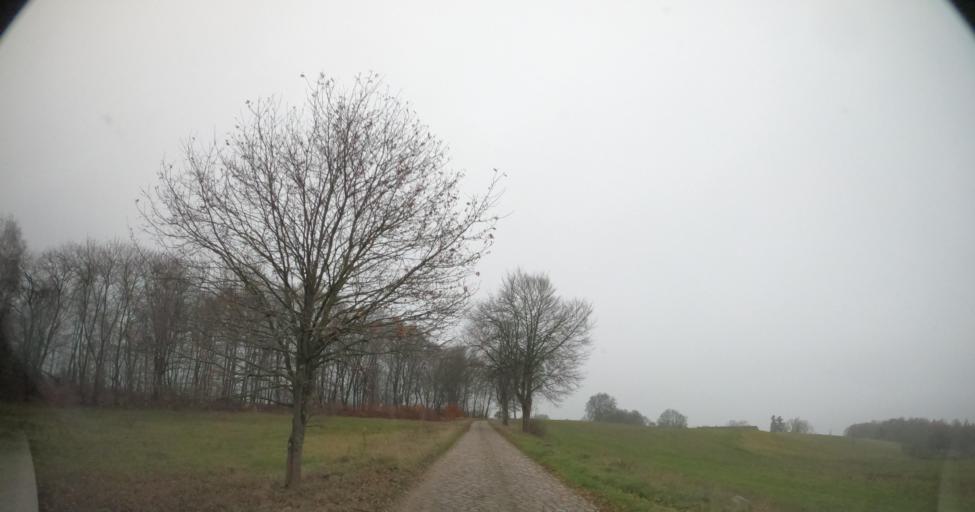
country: PL
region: West Pomeranian Voivodeship
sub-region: Powiat drawski
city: Drawsko Pomorskie
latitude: 53.5447
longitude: 15.7281
